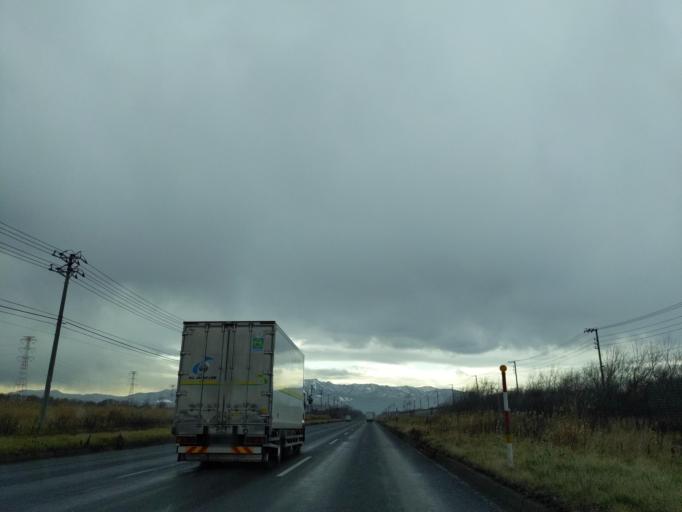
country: JP
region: Hokkaido
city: Ishikari
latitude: 43.1862
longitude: 141.3062
